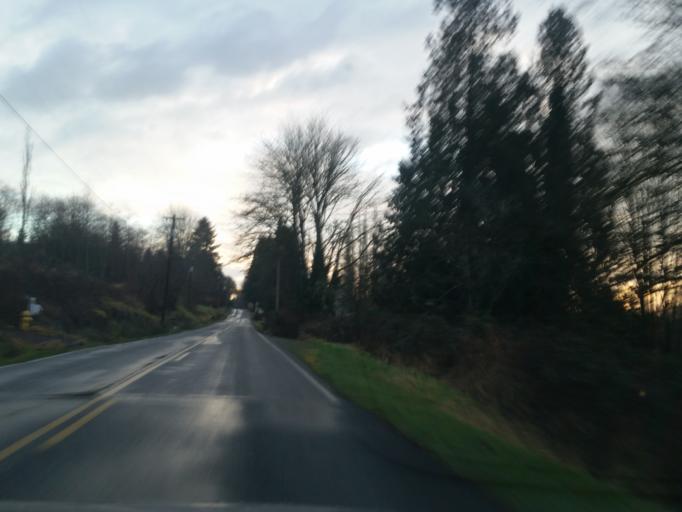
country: US
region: Washington
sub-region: Snohomish County
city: Cathcart
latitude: 47.8470
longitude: -122.0928
